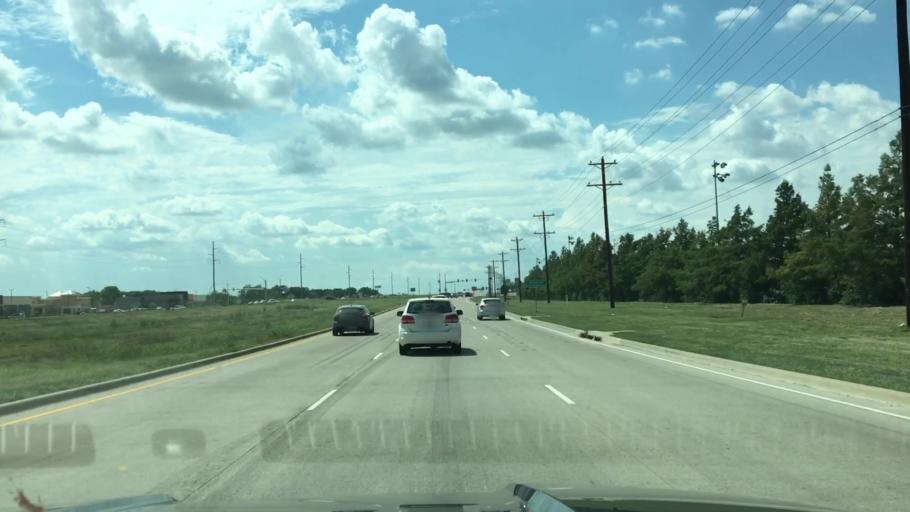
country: US
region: Texas
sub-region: Denton County
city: Roanoke
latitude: 33.0271
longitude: -97.2795
